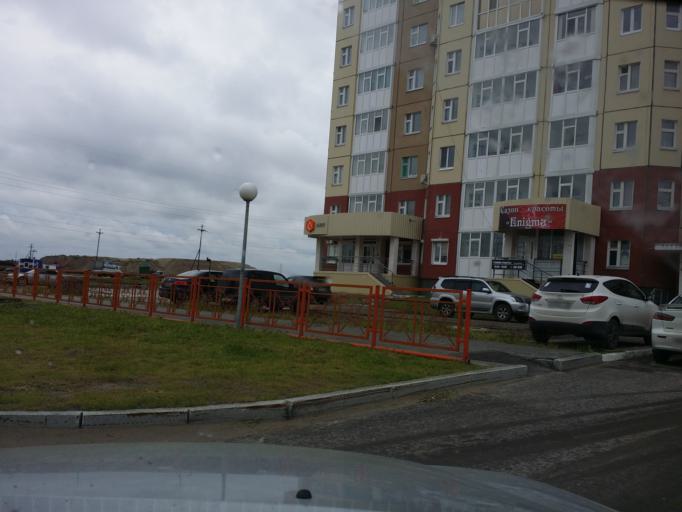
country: RU
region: Khanty-Mansiyskiy Avtonomnyy Okrug
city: Nizhnevartovsk
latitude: 60.9324
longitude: 76.6203
